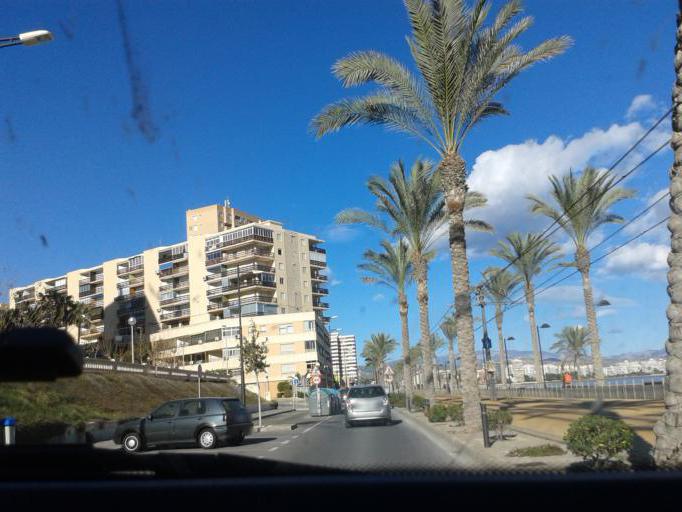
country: ES
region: Valencia
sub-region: Provincia de Alicante
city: el Campello
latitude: 38.4024
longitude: -0.4051
